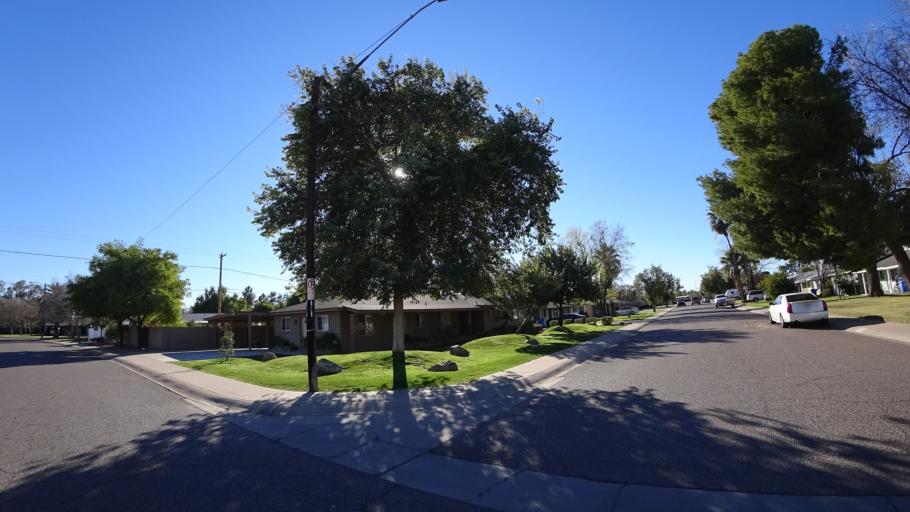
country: US
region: Arizona
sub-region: Maricopa County
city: Phoenix
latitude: 33.5155
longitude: -112.0519
